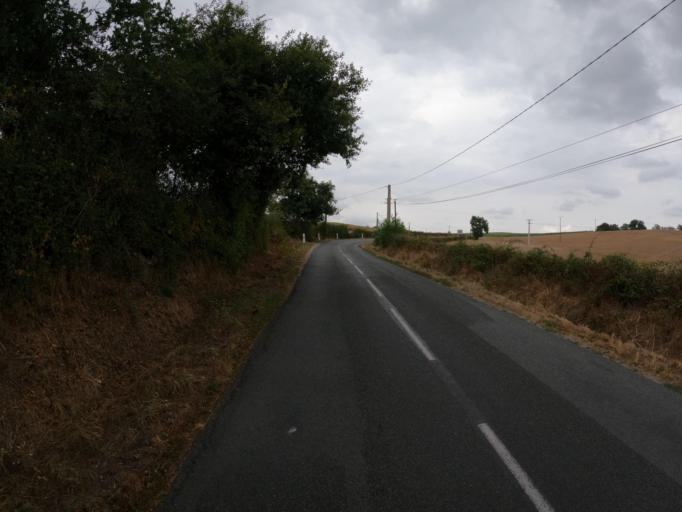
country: FR
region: Pays de la Loire
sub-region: Departement de Maine-et-Loire
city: Le Longeron
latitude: 47.0120
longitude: -1.0748
